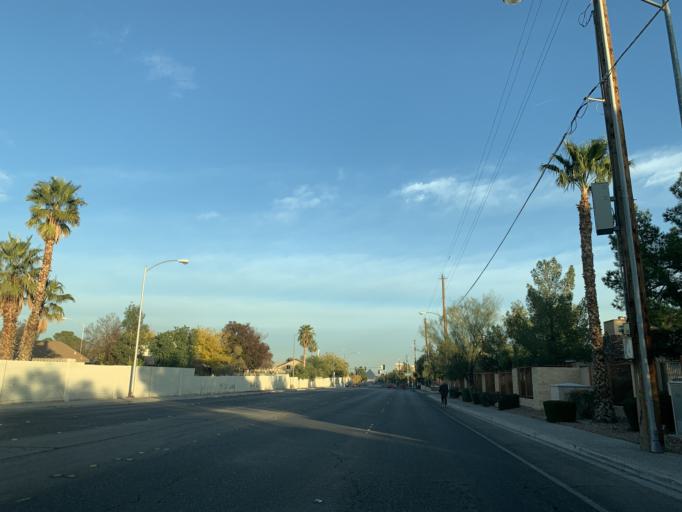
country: US
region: Nevada
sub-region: Clark County
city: Spring Valley
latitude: 36.0925
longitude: -115.2273
